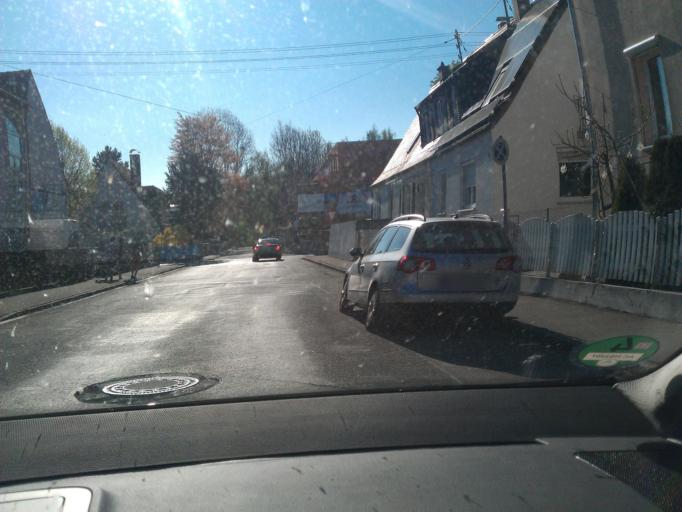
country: DE
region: Bavaria
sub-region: Swabia
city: Friedberg
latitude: 48.3485
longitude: 10.9415
